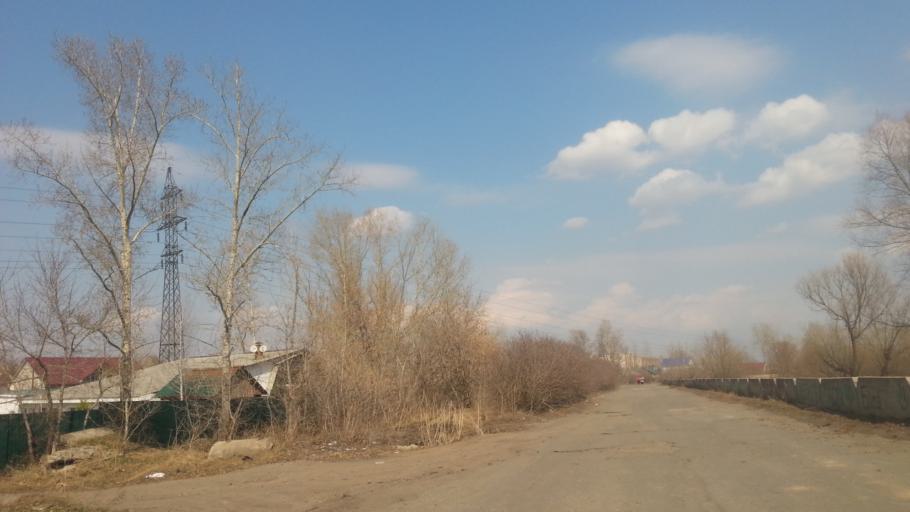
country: RU
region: Altai Krai
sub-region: Gorod Barnaulskiy
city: Barnaul
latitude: 53.3106
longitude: 83.7241
